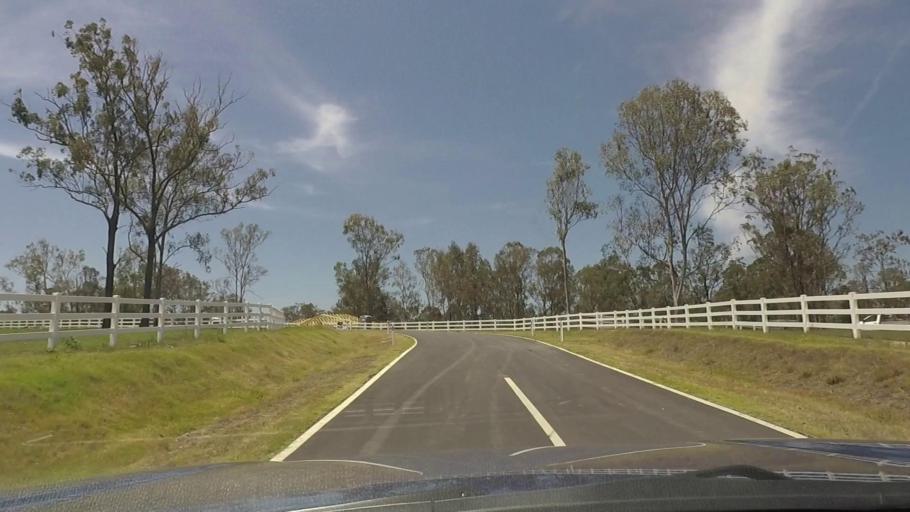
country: AU
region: Queensland
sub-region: Logan
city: North Maclean
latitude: -27.7767
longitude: 153.0359
